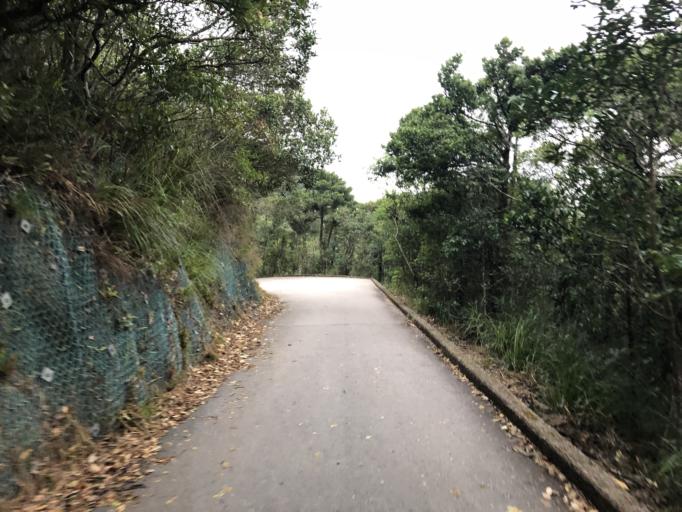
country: HK
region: Wanchai
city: Wan Chai
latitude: 22.2633
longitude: 114.2138
